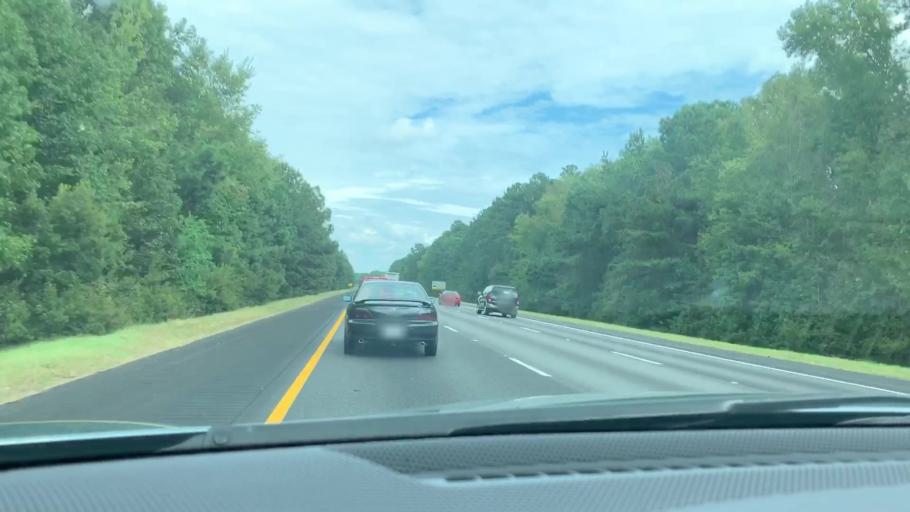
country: US
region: Georgia
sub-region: Chatham County
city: Pooler
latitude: 32.1586
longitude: -81.2284
